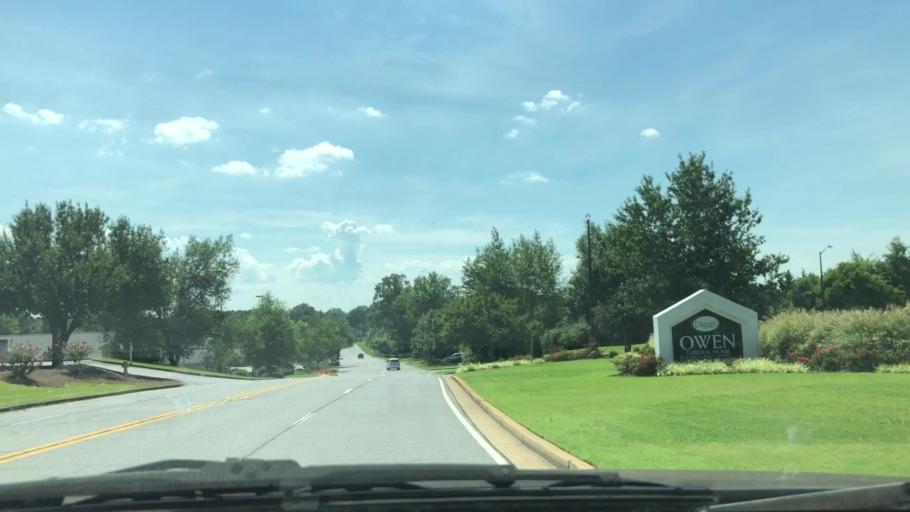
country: US
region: Georgia
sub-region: Bartow County
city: Cartersville
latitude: 34.1929
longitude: -84.7906
